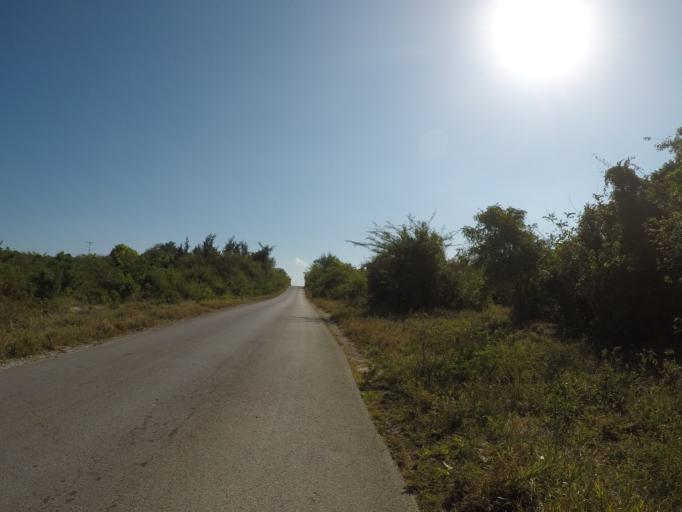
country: TZ
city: Kiwengwa
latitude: -6.1416
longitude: 39.5112
